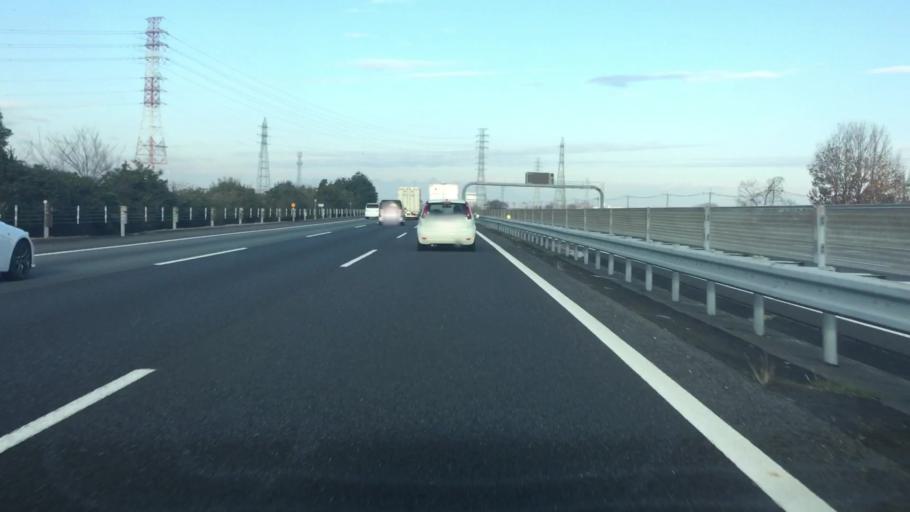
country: JP
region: Saitama
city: Honjo
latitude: 36.2223
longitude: 139.1613
